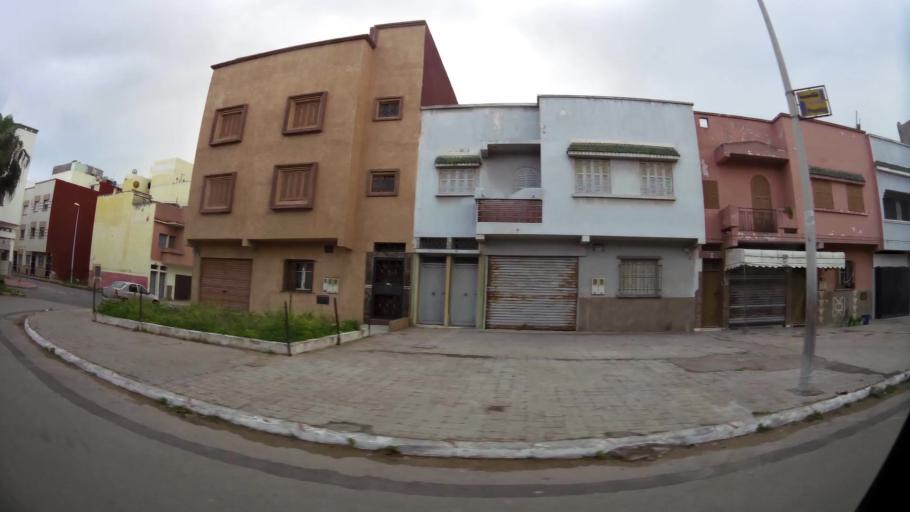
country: MA
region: Doukkala-Abda
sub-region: El-Jadida
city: El Jadida
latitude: 33.2480
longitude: -8.5269
